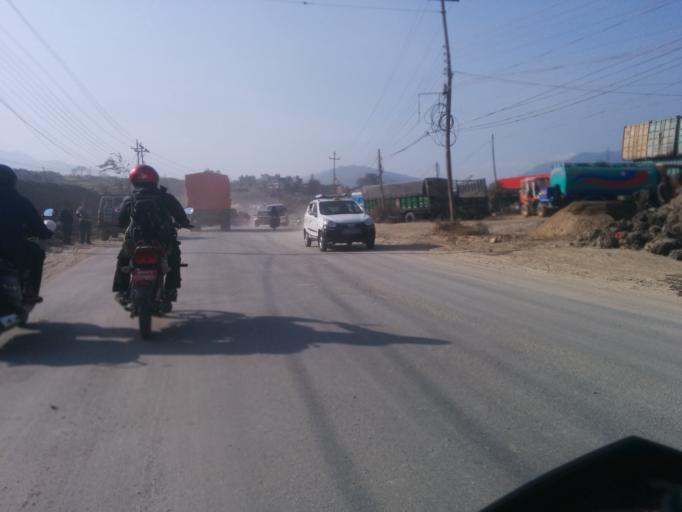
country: NP
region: Central Region
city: Kirtipur
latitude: 27.6853
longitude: 85.2942
